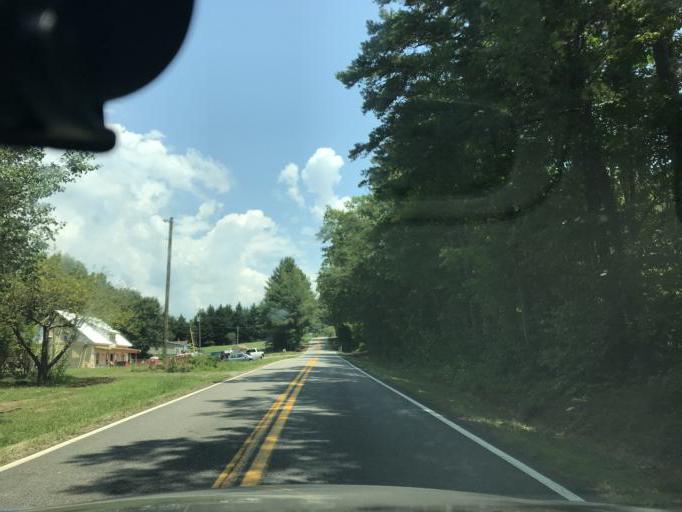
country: US
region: Georgia
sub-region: Forsyth County
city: Cumming
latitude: 34.3117
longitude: -84.1606
